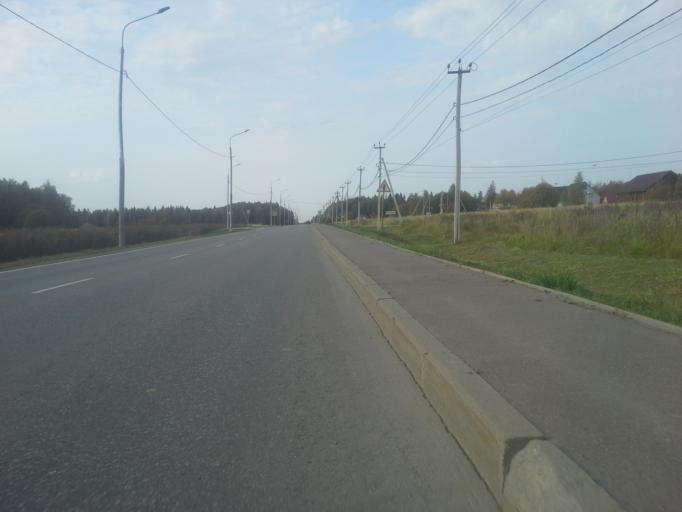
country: RU
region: Moskovskaya
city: Selyatino
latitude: 55.4350
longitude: 36.9578
